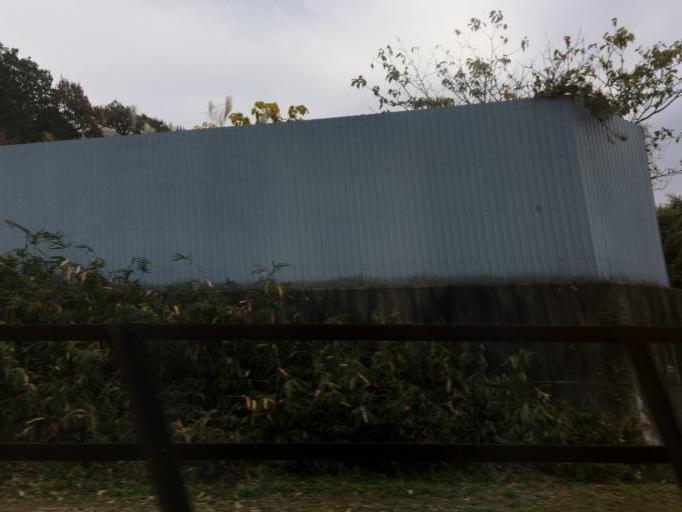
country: JP
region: Tochigi
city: Sano
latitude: 36.3267
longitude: 139.6352
